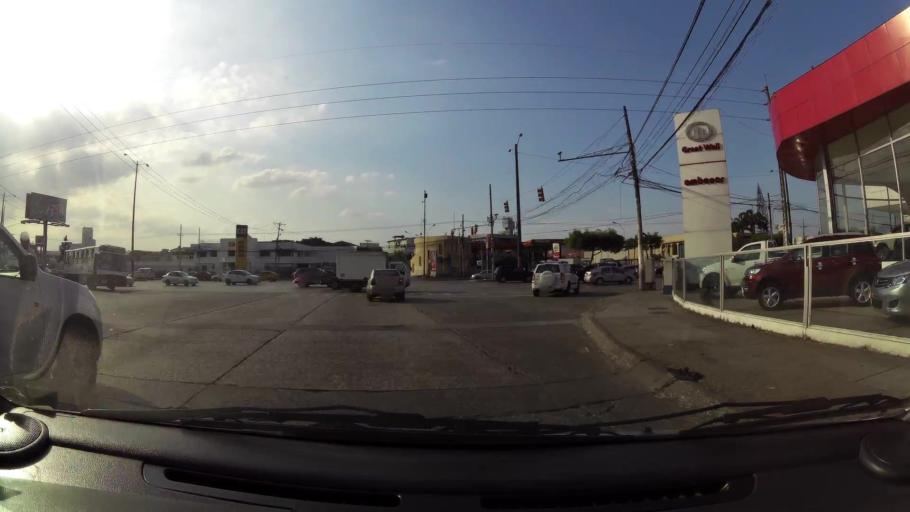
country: EC
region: Guayas
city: Guayaquil
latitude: -2.1483
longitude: -79.9058
